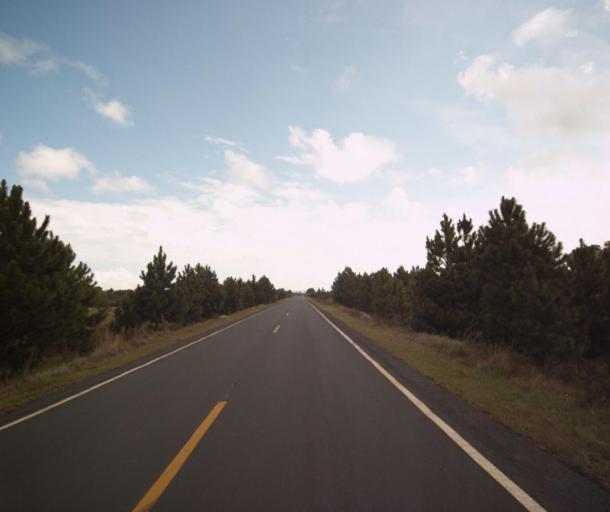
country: BR
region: Rio Grande do Sul
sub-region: Tapes
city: Tapes
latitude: -31.4349
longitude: -51.1933
